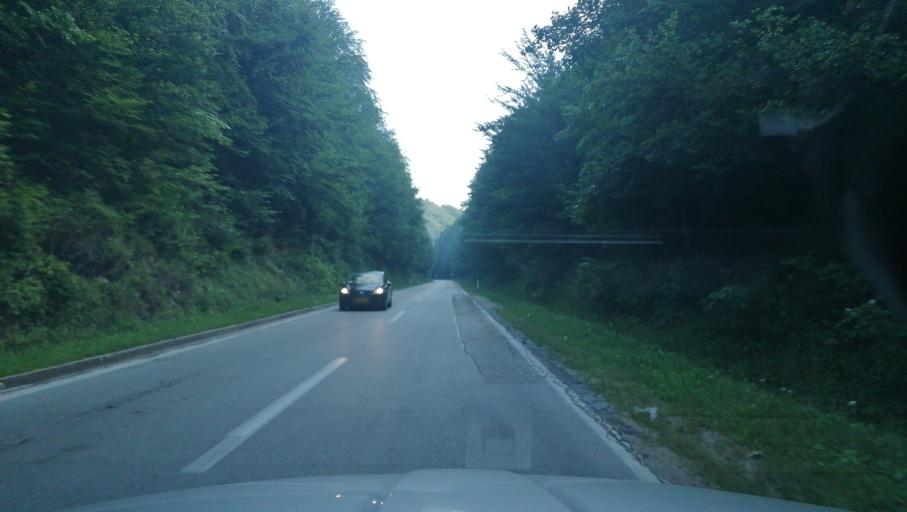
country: BA
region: Federation of Bosnia and Herzegovina
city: Gornji Vakuf
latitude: 43.8825
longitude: 17.5918
